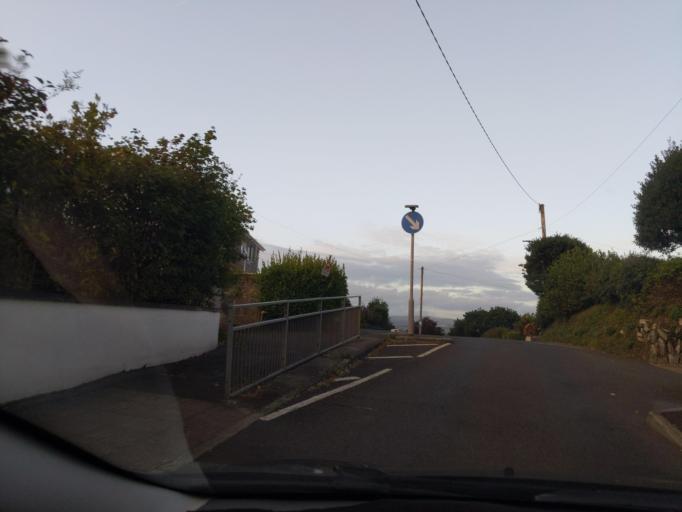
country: GB
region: England
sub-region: Plymouth
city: Plymstock
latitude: 50.3595
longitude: -4.0714
